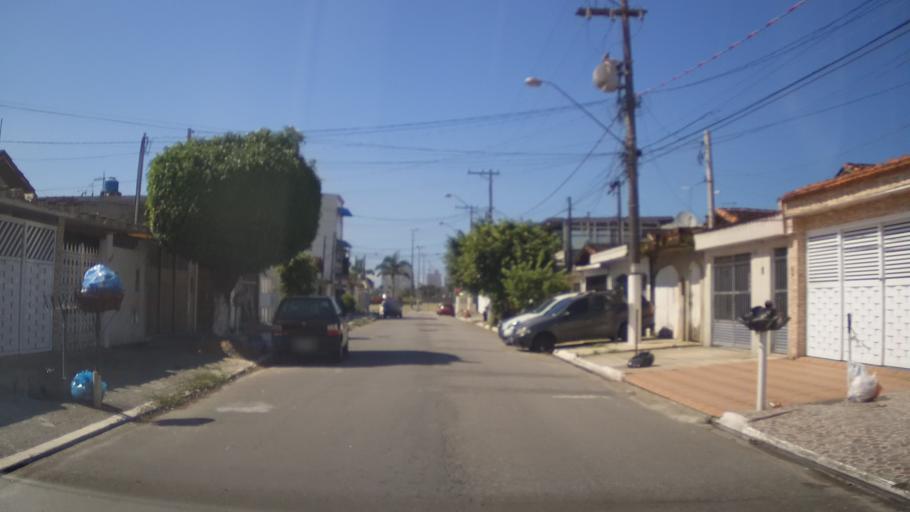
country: BR
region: Sao Paulo
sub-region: Praia Grande
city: Praia Grande
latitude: -24.0172
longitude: -46.4760
